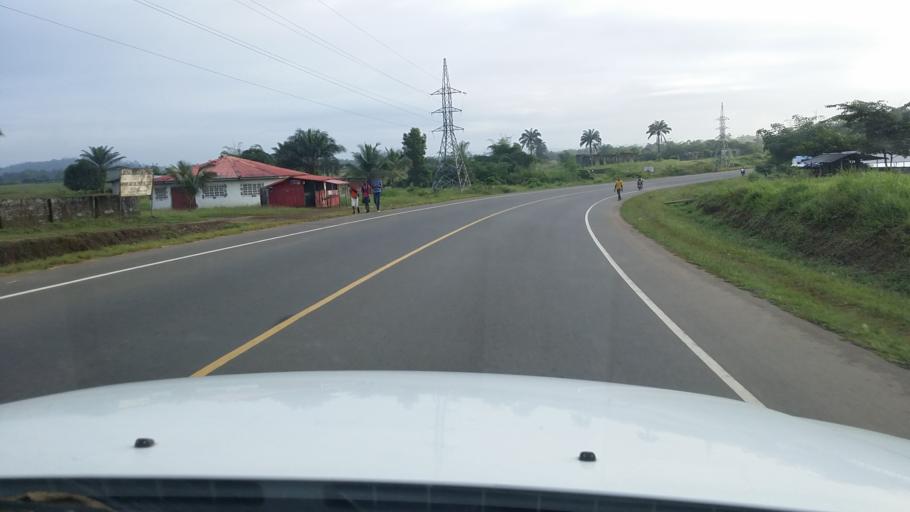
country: LR
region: Montserrado
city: Bensonville City
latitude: 6.3749
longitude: -10.6284
